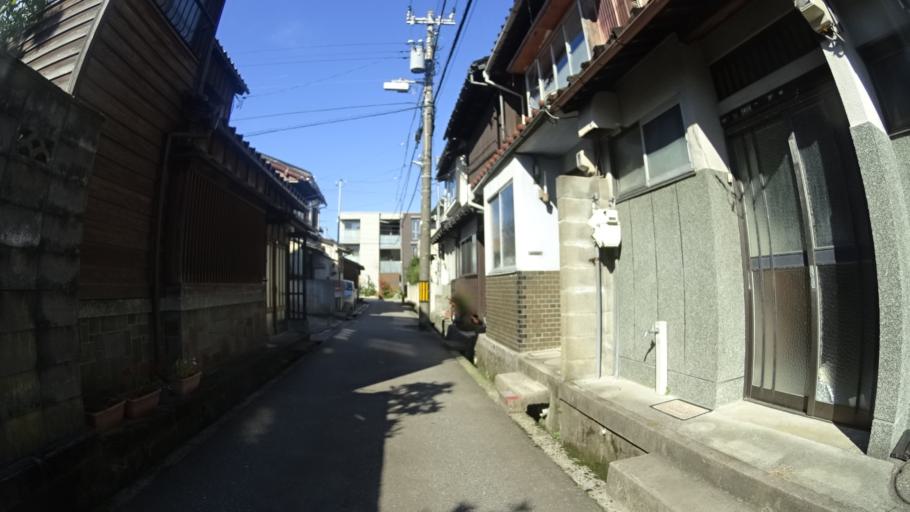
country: JP
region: Ishikawa
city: Kanazawa-shi
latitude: 36.5742
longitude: 136.6625
